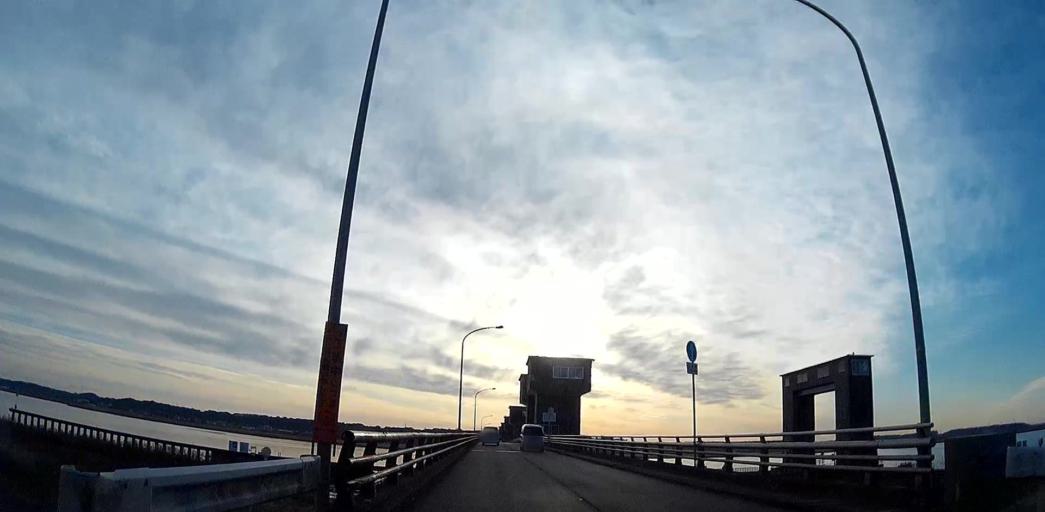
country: JP
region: Chiba
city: Omigawa
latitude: 35.8395
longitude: 140.7062
